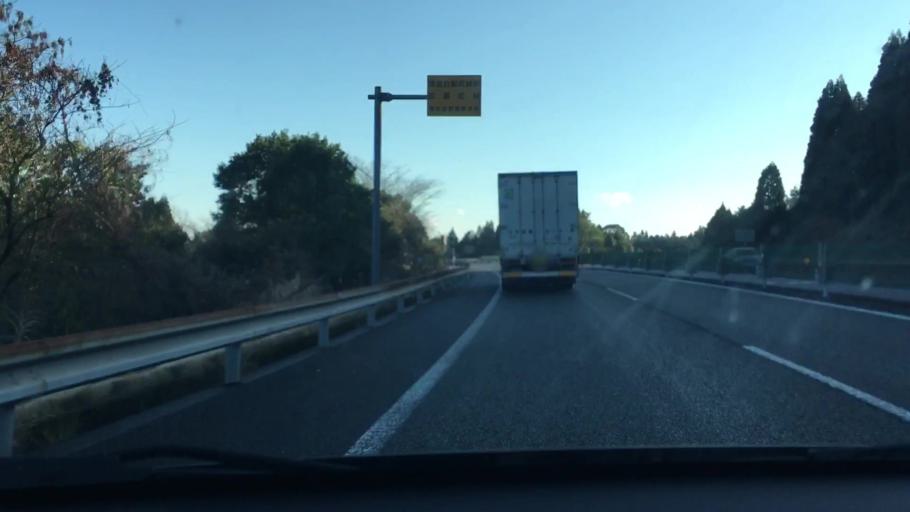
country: JP
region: Kagoshima
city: Kajiki
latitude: 31.8248
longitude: 130.6938
